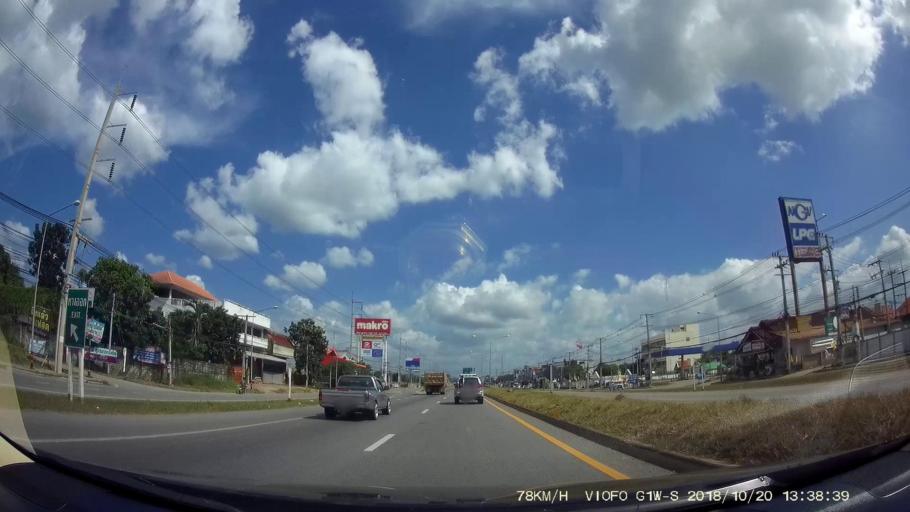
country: TH
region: Khon Kaen
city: Chum Phae
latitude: 16.5519
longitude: 102.0847
